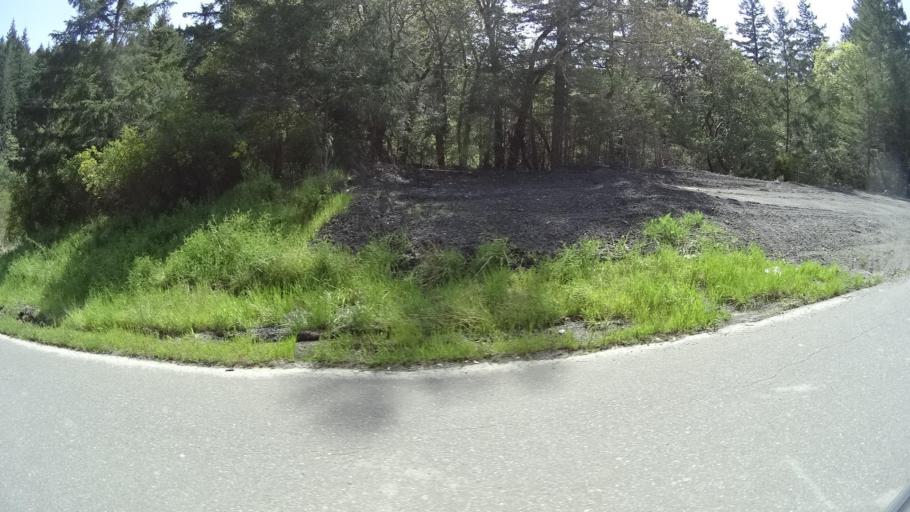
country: US
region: California
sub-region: Humboldt County
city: Redway
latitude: 40.3678
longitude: -123.7294
